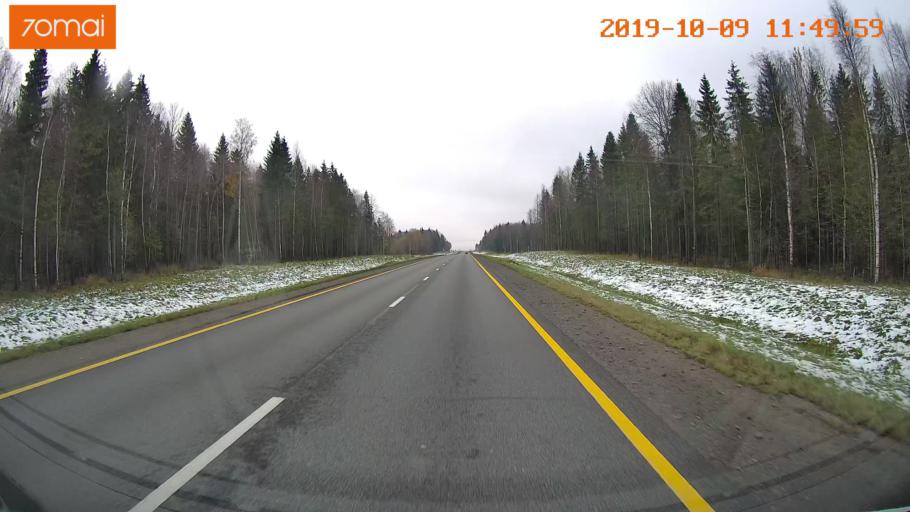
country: RU
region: Vologda
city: Gryazovets
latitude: 58.8113
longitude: 40.2391
